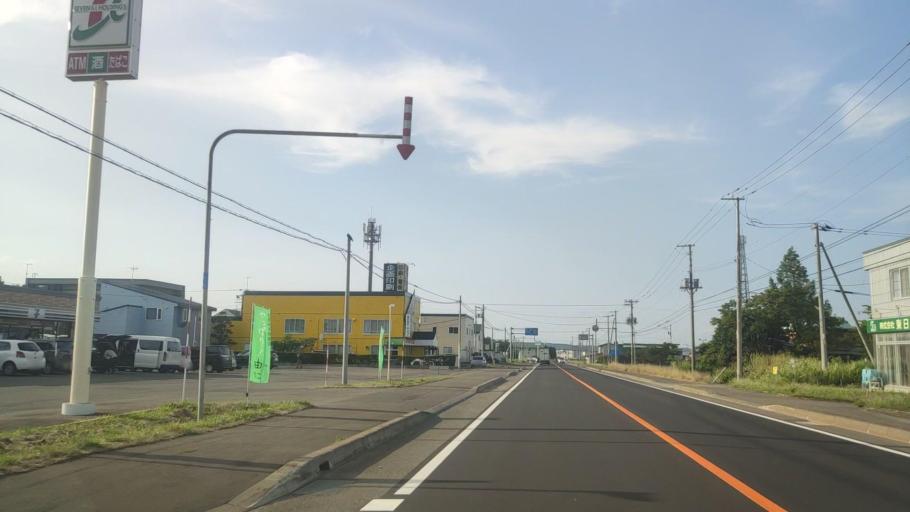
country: JP
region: Hokkaido
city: Iwamizawa
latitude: 43.0117
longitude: 141.7889
